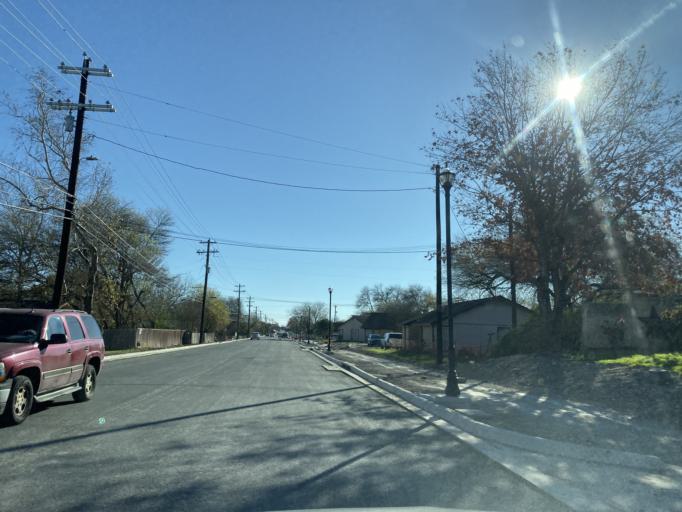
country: US
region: Texas
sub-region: Hays County
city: Kyle
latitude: 29.9980
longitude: -97.8755
